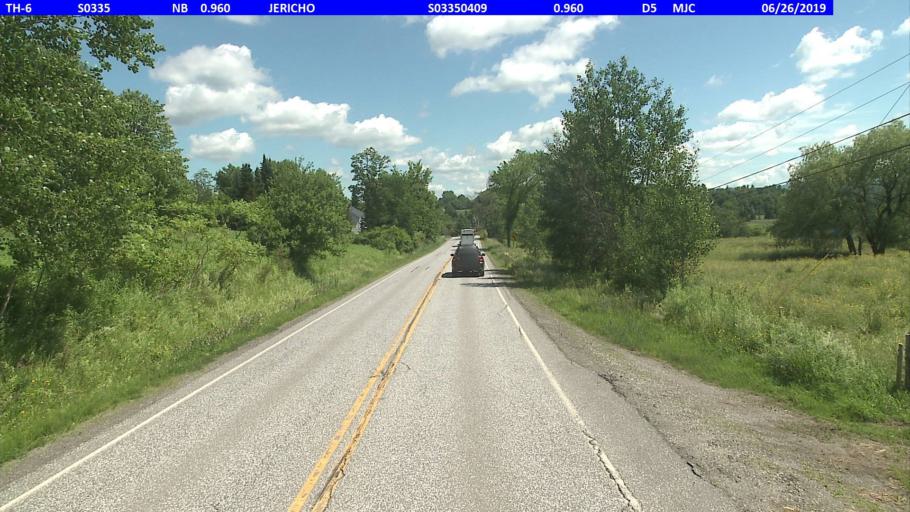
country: US
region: Vermont
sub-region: Chittenden County
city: Jericho
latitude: 44.4787
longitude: -73.0187
